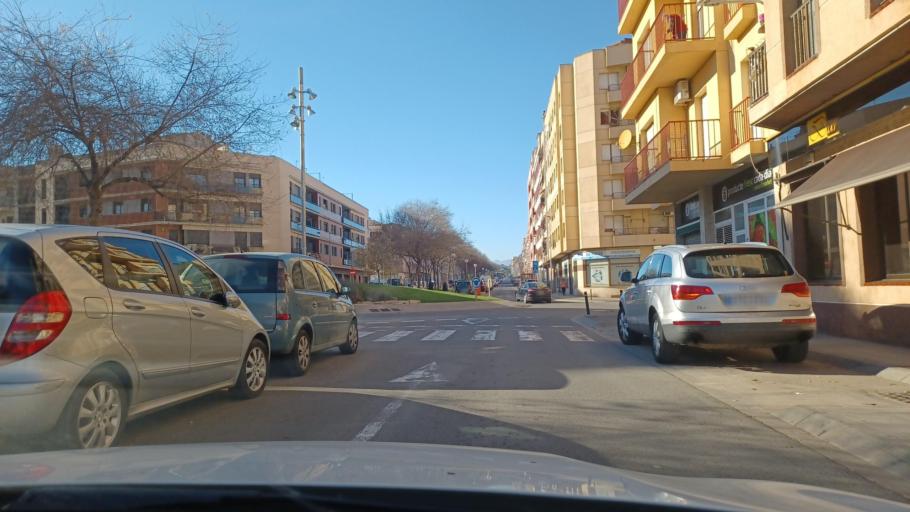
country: ES
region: Catalonia
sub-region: Provincia de Tarragona
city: Amposta
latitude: 40.7039
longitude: 0.5793
